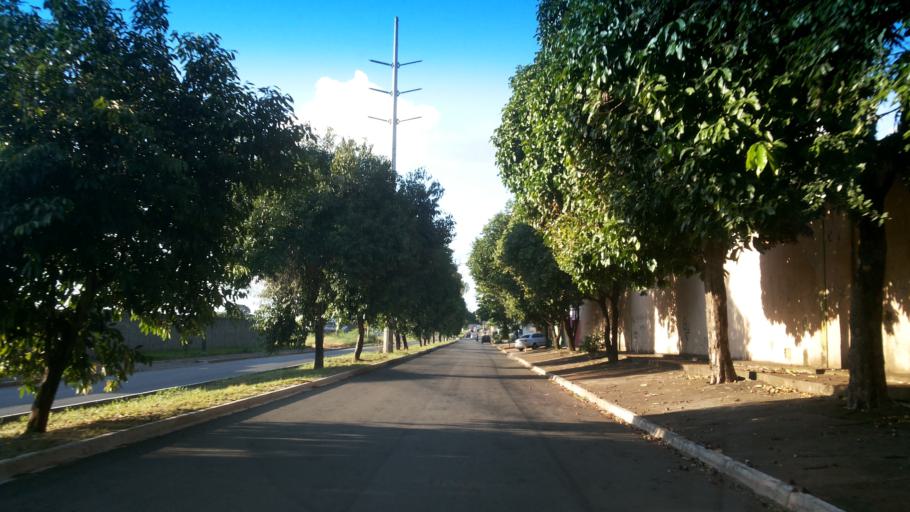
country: BR
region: Goias
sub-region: Goiania
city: Goiania
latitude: -16.7335
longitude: -49.3091
